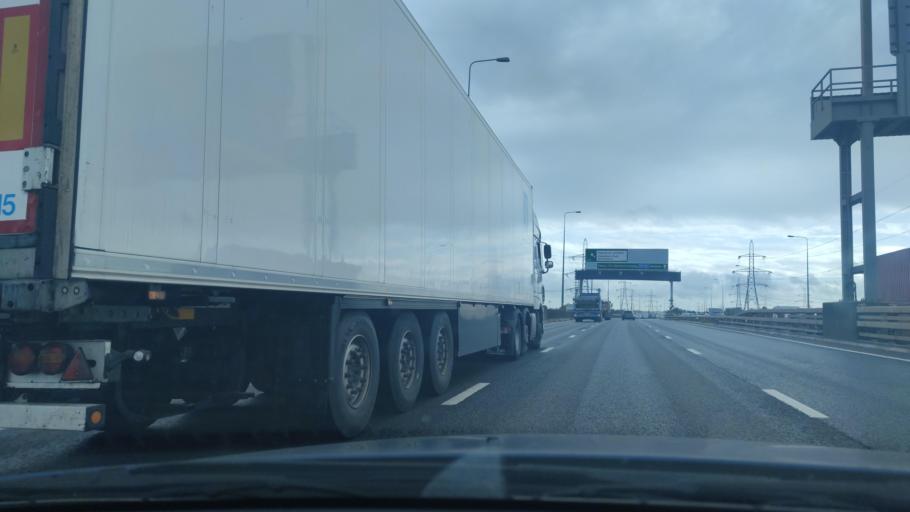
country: GB
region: England
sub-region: Greater London
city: Dagenham
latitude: 51.5244
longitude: 0.1510
